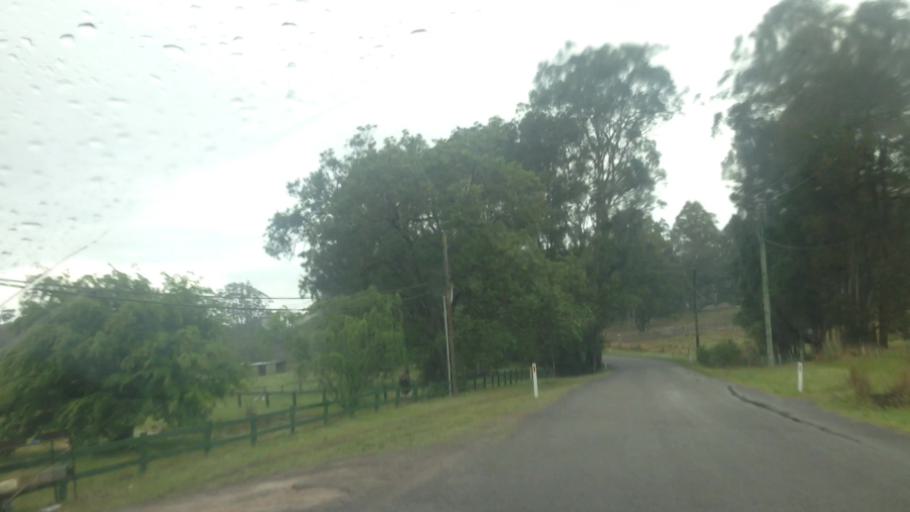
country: AU
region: New South Wales
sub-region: Wyong Shire
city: Little Jilliby
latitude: -33.2098
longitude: 151.3697
